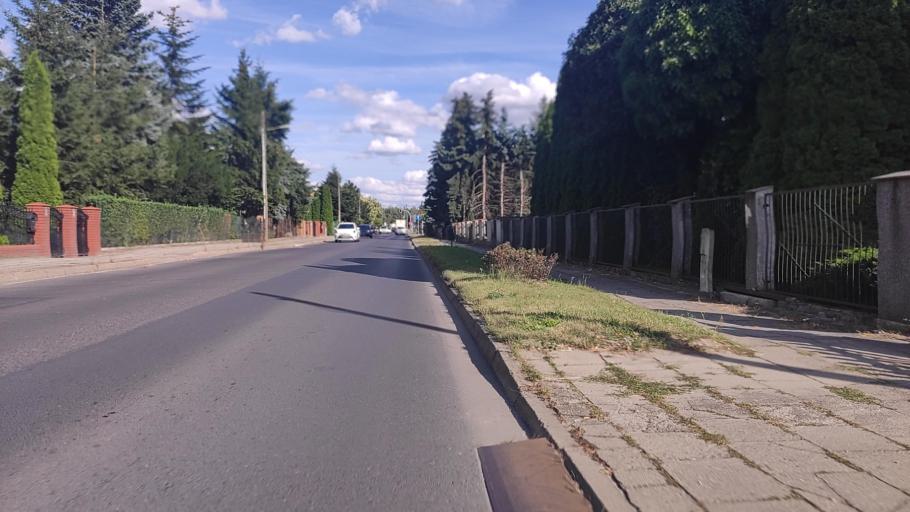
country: PL
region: Greater Poland Voivodeship
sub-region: Powiat poznanski
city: Swarzedz
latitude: 52.3971
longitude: 17.0744
